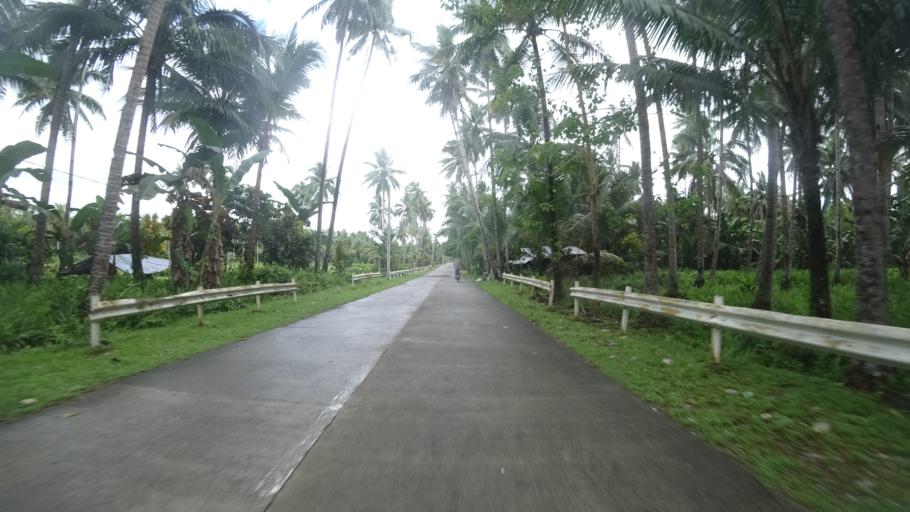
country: PH
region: Eastern Visayas
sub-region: Province of Leyte
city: Bugho
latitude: 10.8309
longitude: 124.9362
